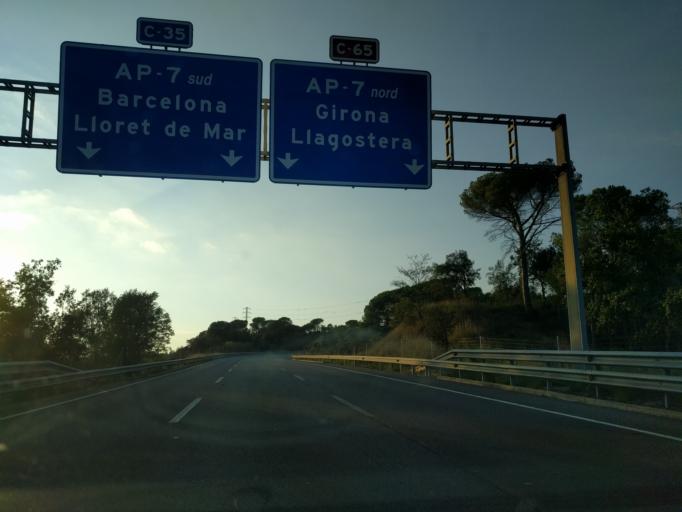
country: ES
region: Catalonia
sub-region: Provincia de Girona
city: Llagostera
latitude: 41.8285
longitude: 2.9404
